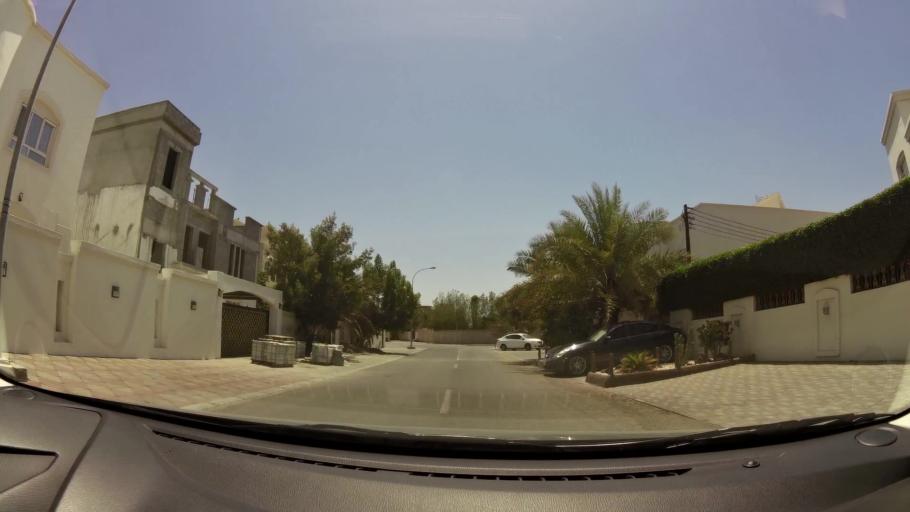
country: OM
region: Muhafazat Masqat
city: As Sib al Jadidah
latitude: 23.6162
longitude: 58.2269
